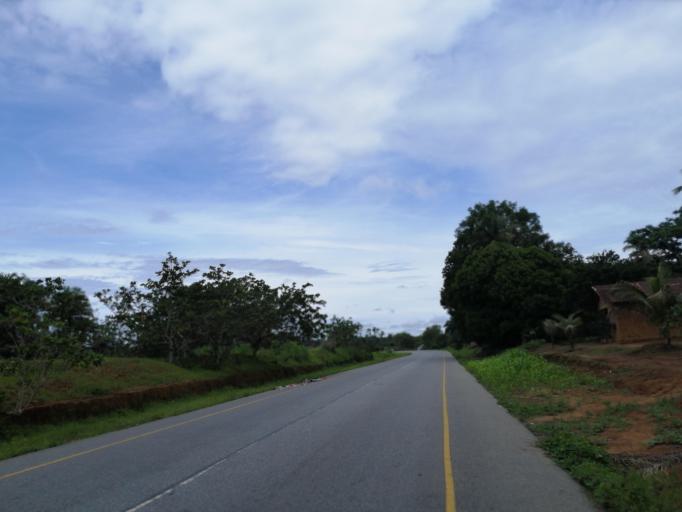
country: SL
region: Northern Province
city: Port Loko
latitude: 8.7556
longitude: -12.9145
